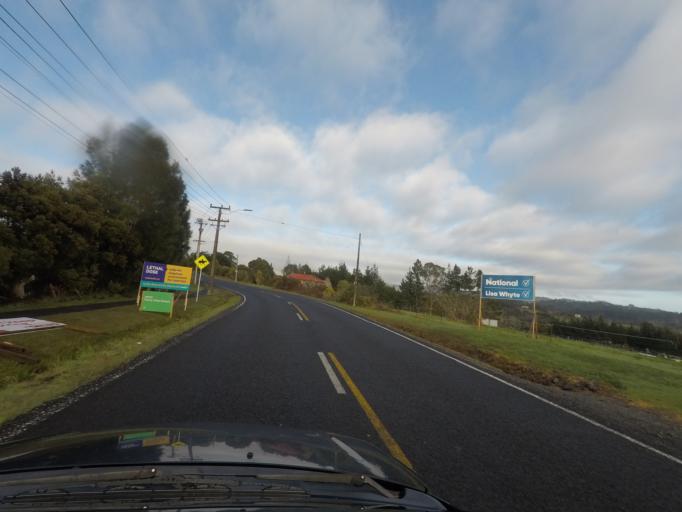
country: NZ
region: Auckland
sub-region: Auckland
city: Waitakere
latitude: -36.9006
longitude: 174.6148
